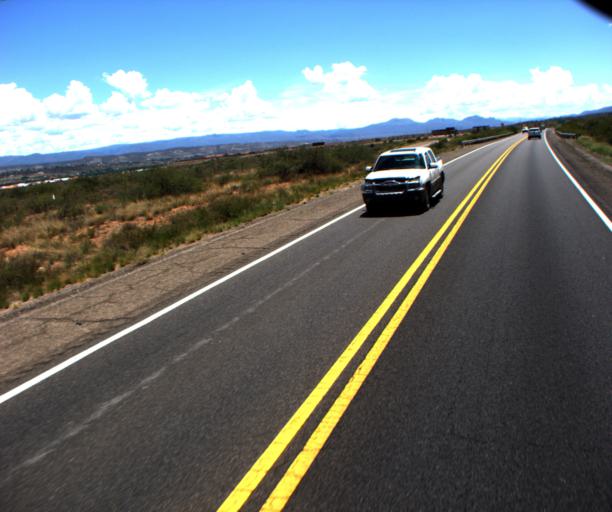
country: US
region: Arizona
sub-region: Yavapai County
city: Camp Verde
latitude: 34.6141
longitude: -111.9150
